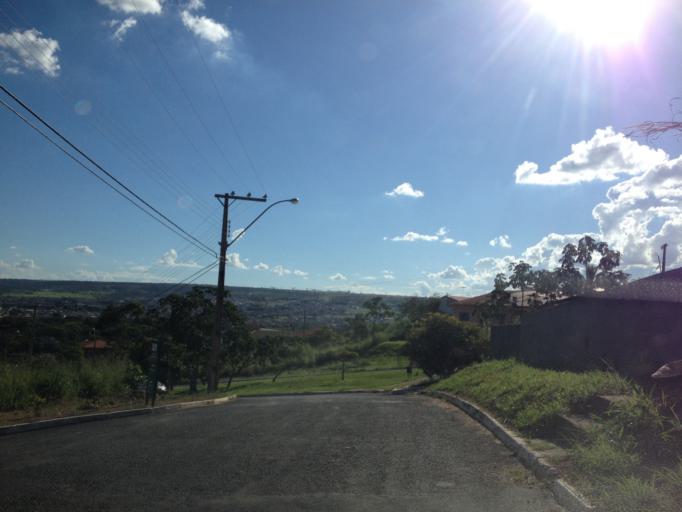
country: BR
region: Federal District
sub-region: Brasilia
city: Brasilia
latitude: -15.8885
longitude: -47.7569
